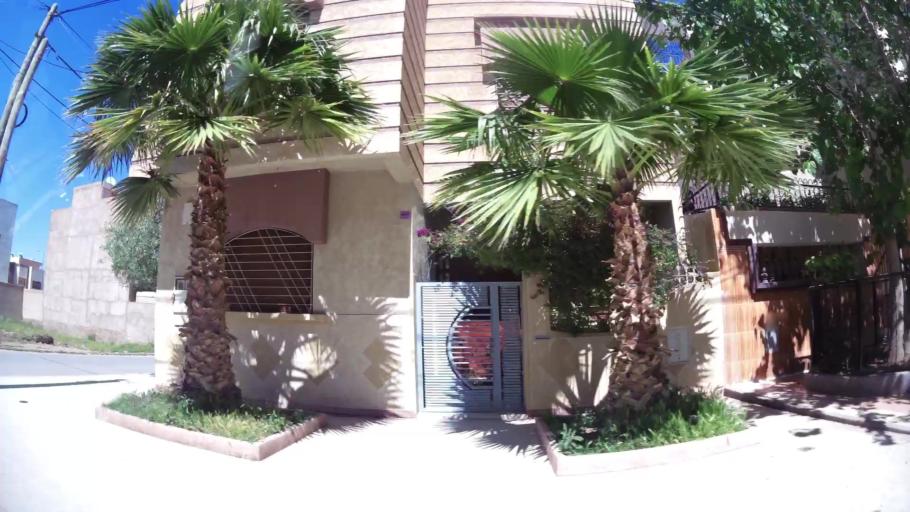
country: MA
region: Oriental
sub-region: Oujda-Angad
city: Oujda
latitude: 34.6662
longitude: -1.8786
